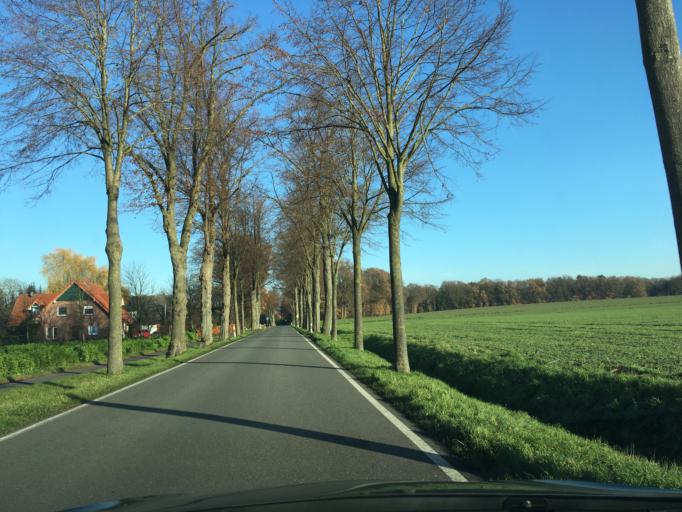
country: DE
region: North Rhine-Westphalia
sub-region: Regierungsbezirk Munster
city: Vreden
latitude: 52.1062
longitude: 6.8716
